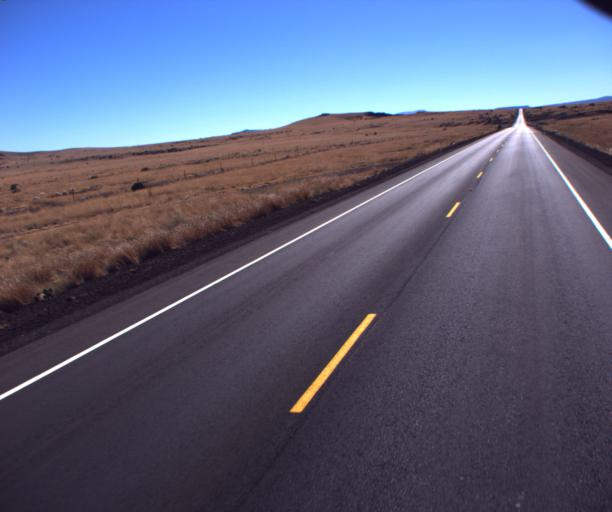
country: US
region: Arizona
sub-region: Apache County
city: Springerville
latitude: 34.2603
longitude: -109.3562
